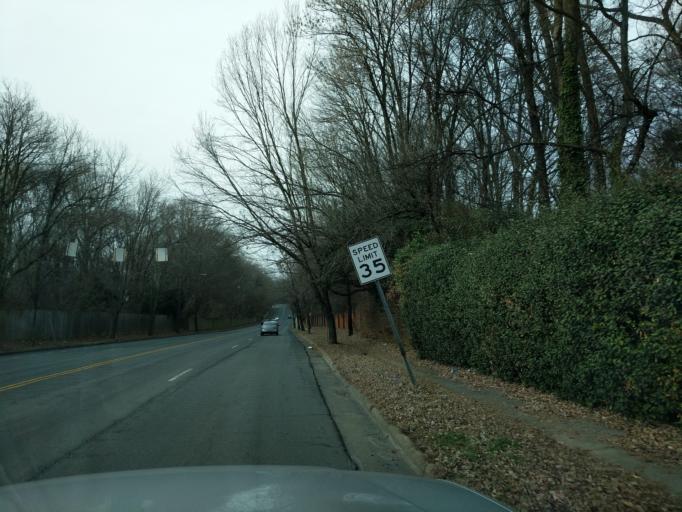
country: US
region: North Carolina
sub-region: Mecklenburg County
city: Charlotte
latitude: 35.1680
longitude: -80.8233
